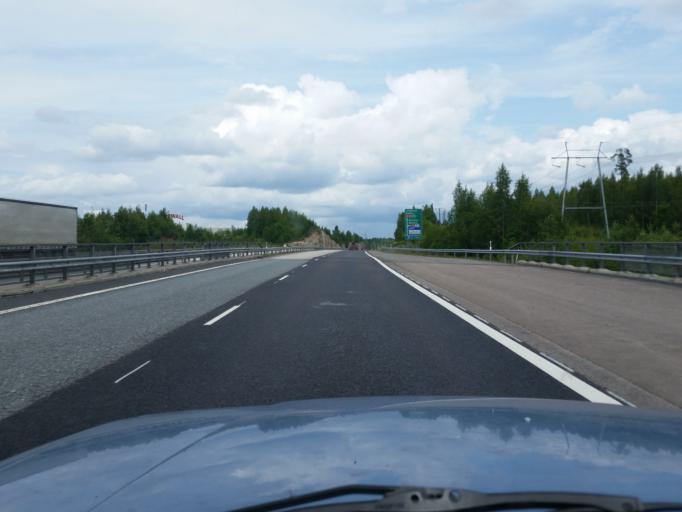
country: FI
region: Paijanne Tavastia
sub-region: Lahti
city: Lahti
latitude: 60.9603
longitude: 25.7018
